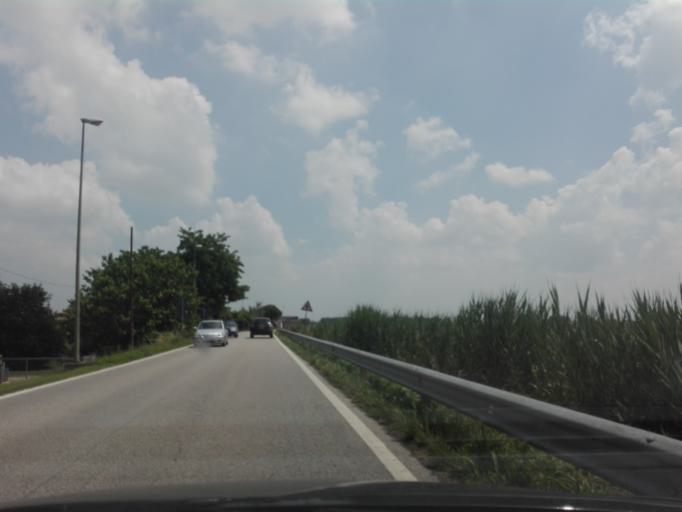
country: IT
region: Veneto
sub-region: Provincia di Rovigo
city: Adria
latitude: 45.0601
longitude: 12.0142
